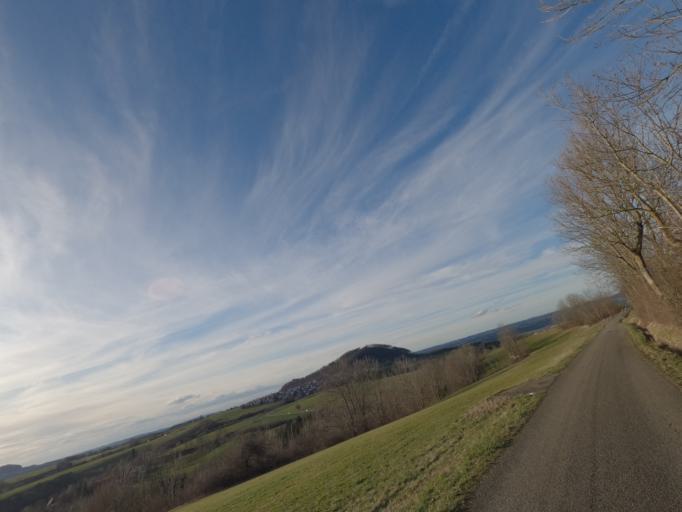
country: DE
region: Baden-Wuerttemberg
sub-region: Regierungsbezirk Stuttgart
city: Waldstetten
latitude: 48.7418
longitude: 9.8103
